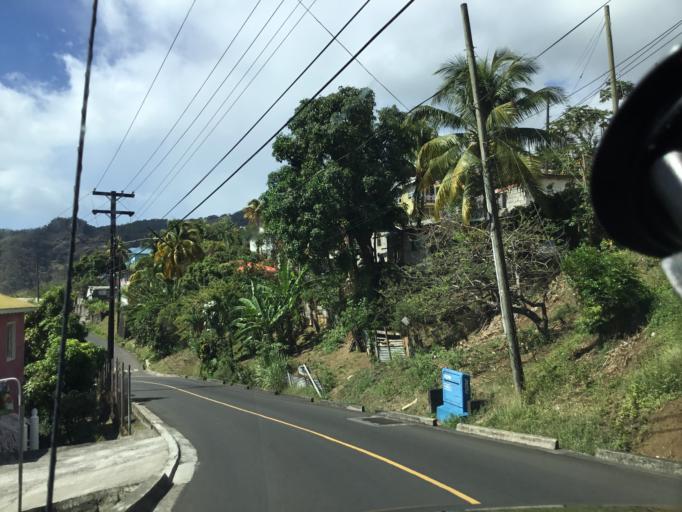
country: VC
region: Saint Andrew
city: Layou
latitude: 13.1910
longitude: -61.2463
